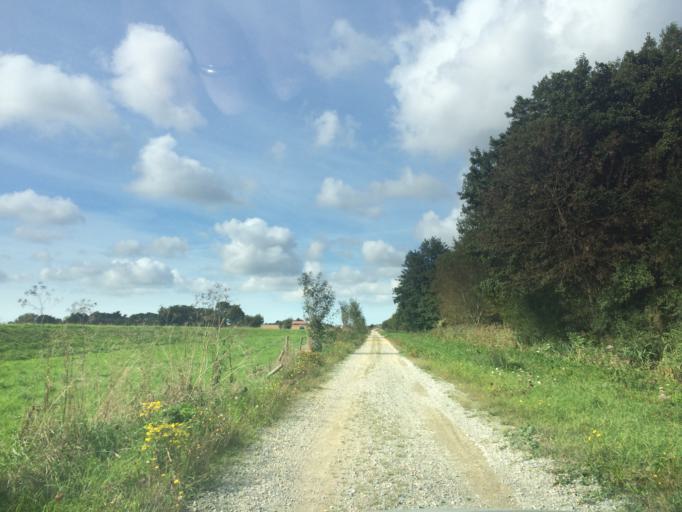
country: FR
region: Pays de la Loire
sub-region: Departement de la Loire-Atlantique
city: Chemere
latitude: 47.1257
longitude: -1.9241
